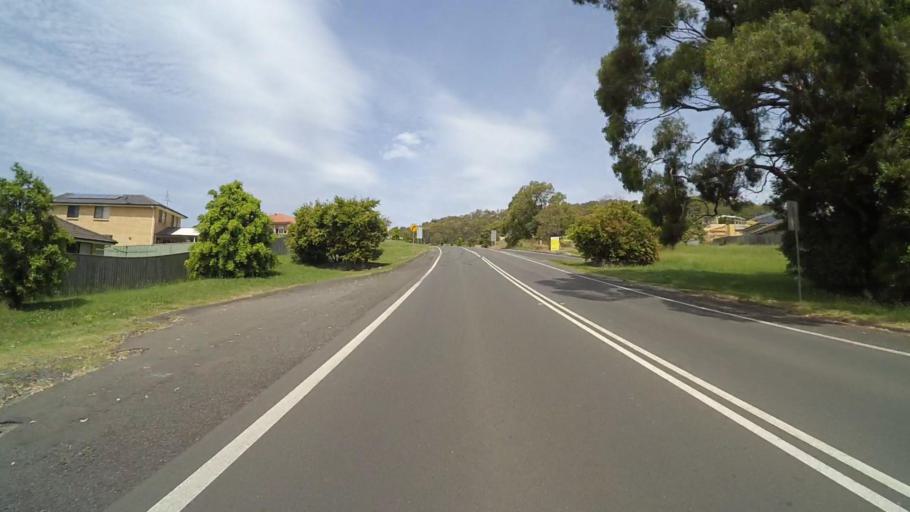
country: AU
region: New South Wales
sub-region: Shellharbour
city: Albion Park Rail
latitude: -34.5934
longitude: 150.7823
